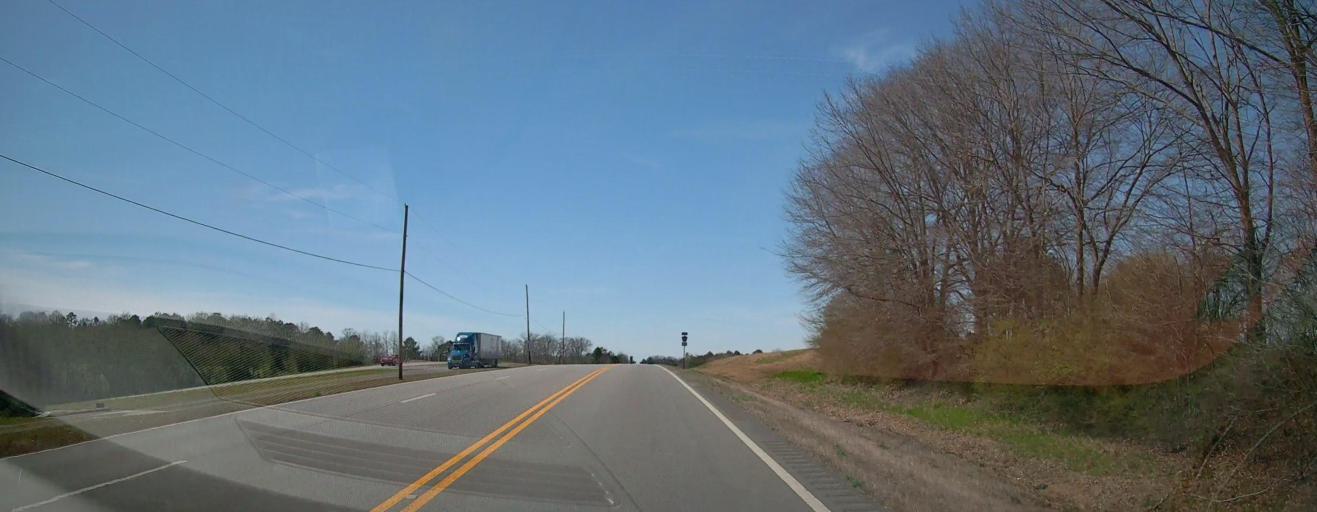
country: US
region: Alabama
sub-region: Blount County
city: Blountsville
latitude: 34.1737
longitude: -86.5550
